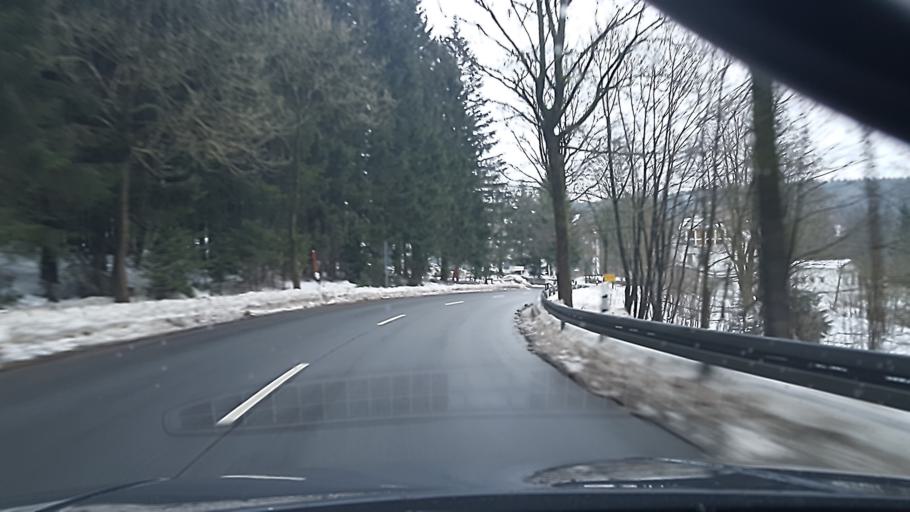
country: DE
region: Lower Saxony
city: Clausthal-Zellerfeld
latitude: 51.8498
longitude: 10.3288
